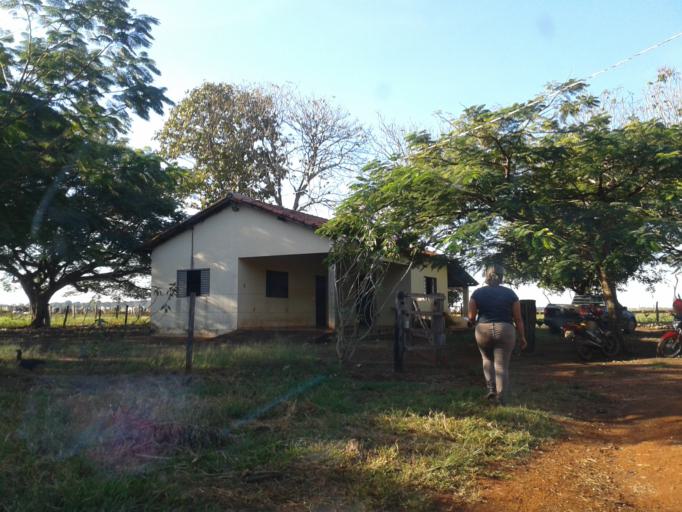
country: BR
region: Minas Gerais
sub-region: Santa Vitoria
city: Santa Vitoria
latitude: -19.0010
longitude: -50.3433
